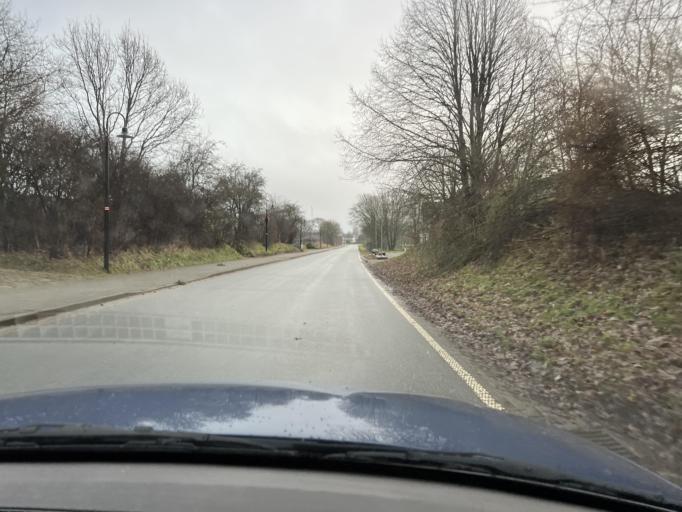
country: DE
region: Schleswig-Holstein
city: Lohe-Rickelshof
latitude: 54.2144
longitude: 9.0713
